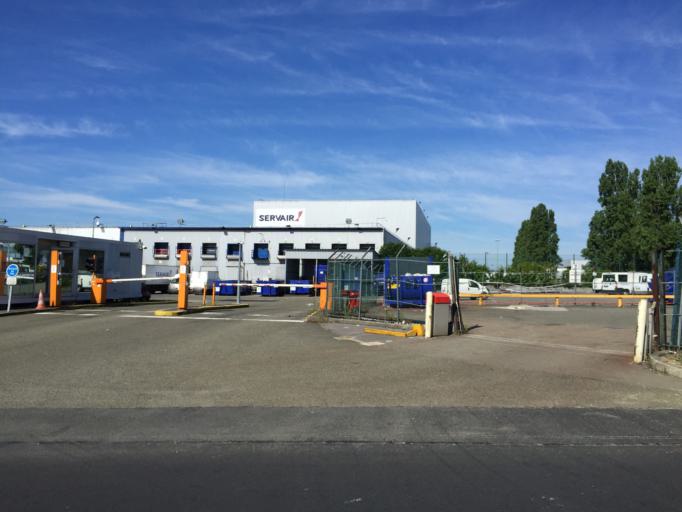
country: FR
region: Ile-de-France
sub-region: Departement du Val-d'Oise
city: Roissy-en-France
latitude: 49.0038
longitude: 2.5526
